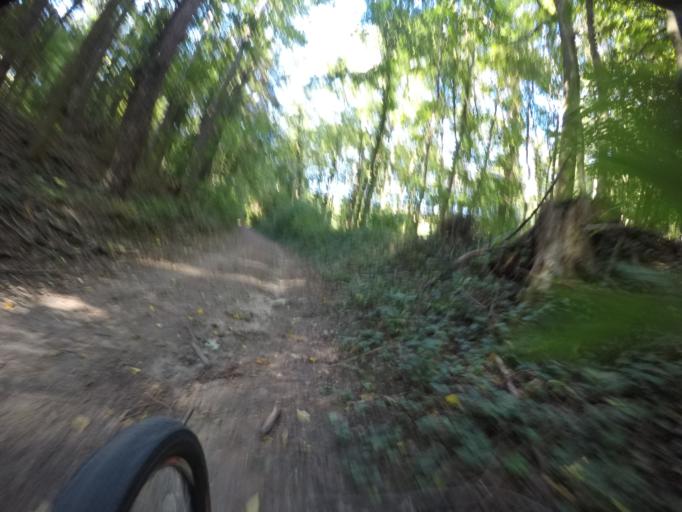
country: AT
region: Lower Austria
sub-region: Politischer Bezirk Bruck an der Leitha
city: Mannersdorf am Leithagebirge
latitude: 47.9595
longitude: 16.6139
